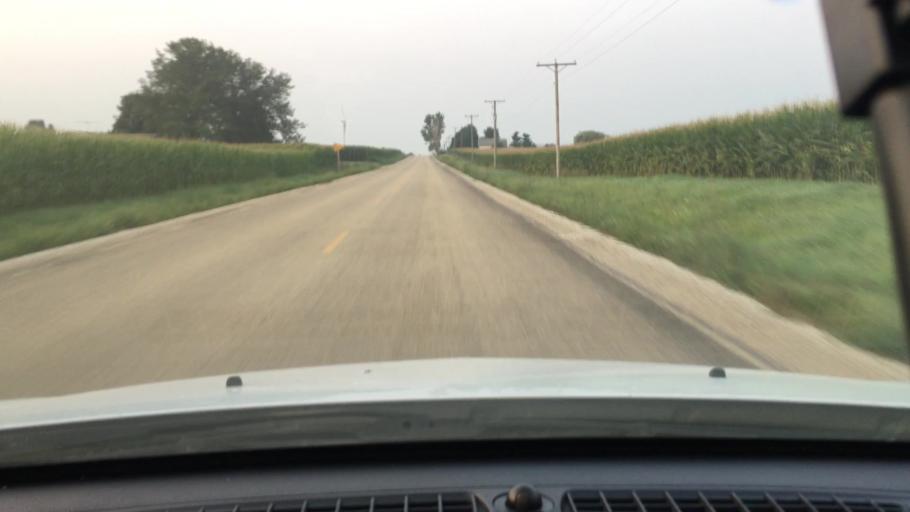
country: US
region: Illinois
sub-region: DeKalb County
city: Waterman
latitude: 41.8394
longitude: -88.7734
